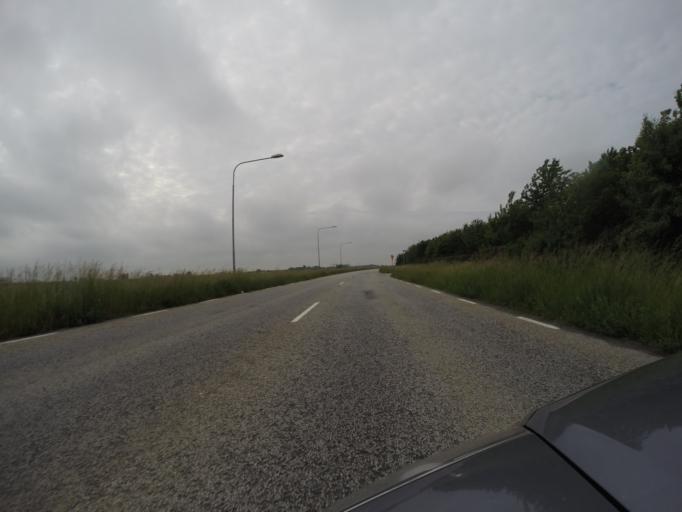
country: SE
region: Skane
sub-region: Lomma Kommun
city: Lomma
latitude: 55.6799
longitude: 13.0958
